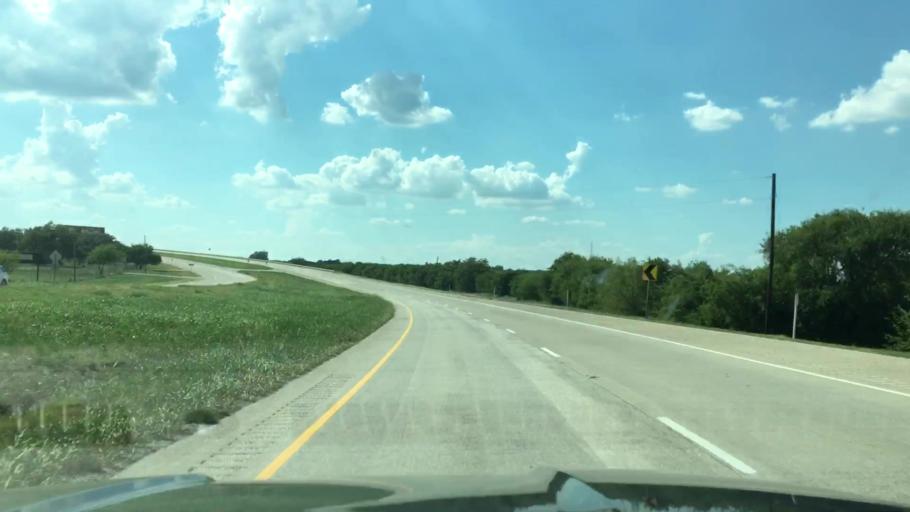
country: US
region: Texas
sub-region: Wise County
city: Rhome
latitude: 33.0455
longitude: -97.4542
